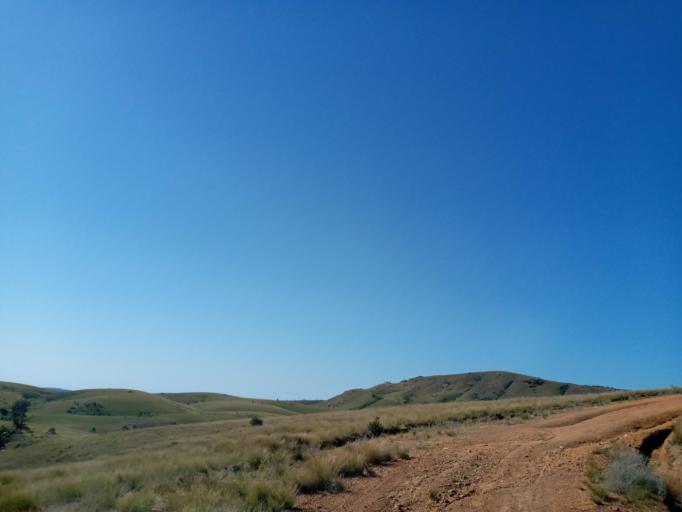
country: MG
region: Anosy
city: Fort Dauphin
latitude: -24.9093
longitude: 47.0731
